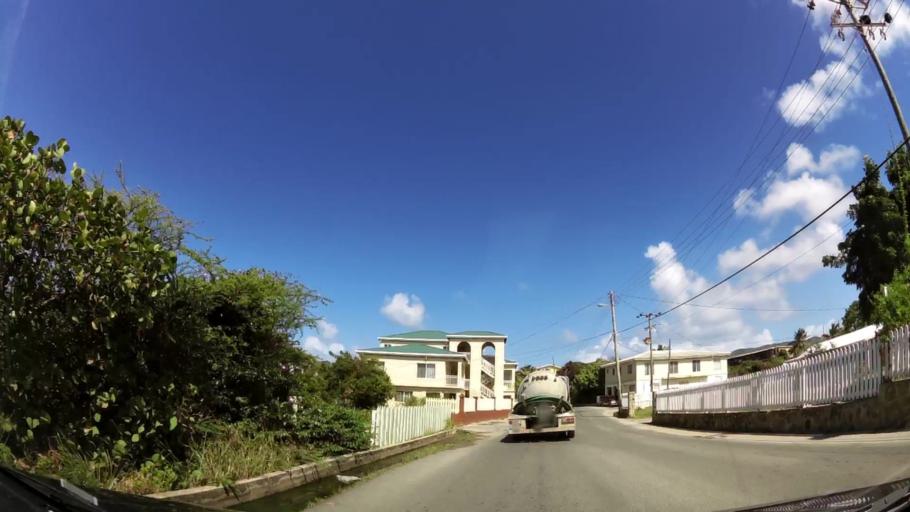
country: VG
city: Tortola
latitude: 18.4514
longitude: -64.4306
